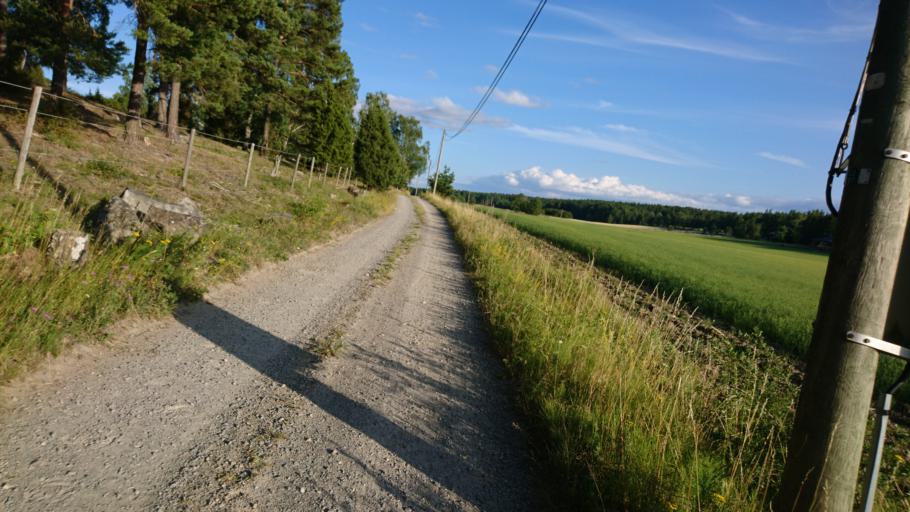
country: SE
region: Soedermanland
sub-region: Strangnas Kommun
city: Stallarholmen
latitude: 59.3970
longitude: 17.2749
